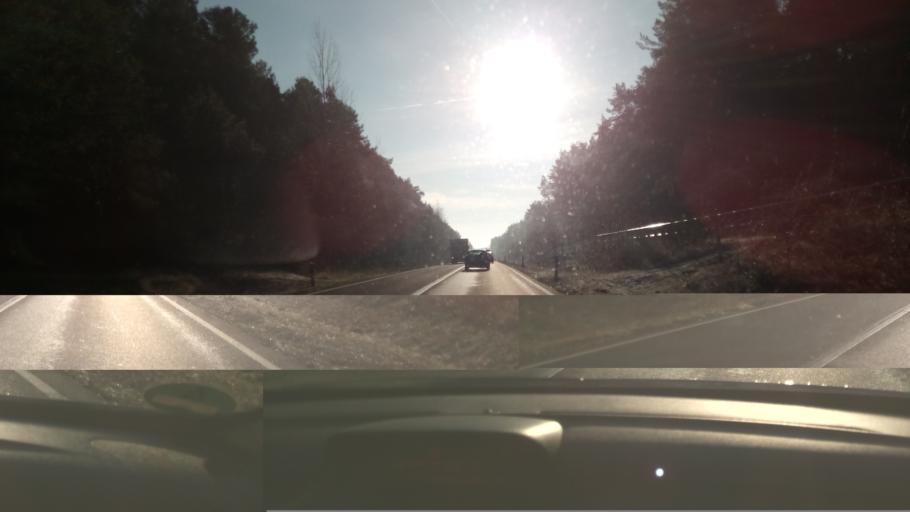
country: DE
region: Mecklenburg-Vorpommern
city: Neustrelitz
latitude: 53.3564
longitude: 13.0959
